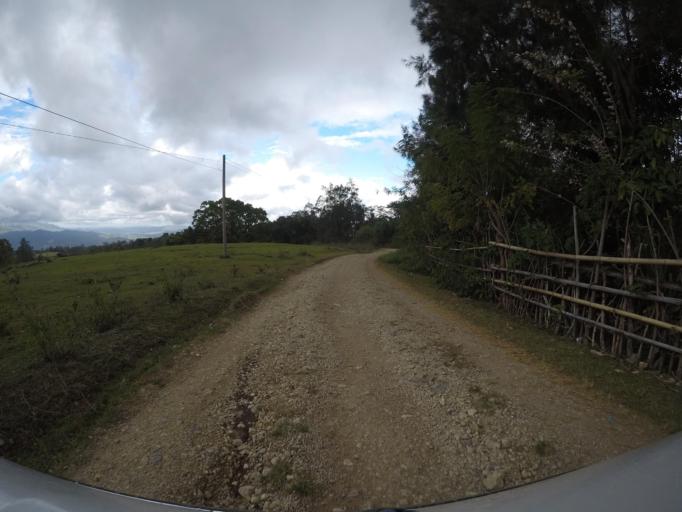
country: TL
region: Baucau
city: Venilale
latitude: -8.6714
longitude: 126.6287
